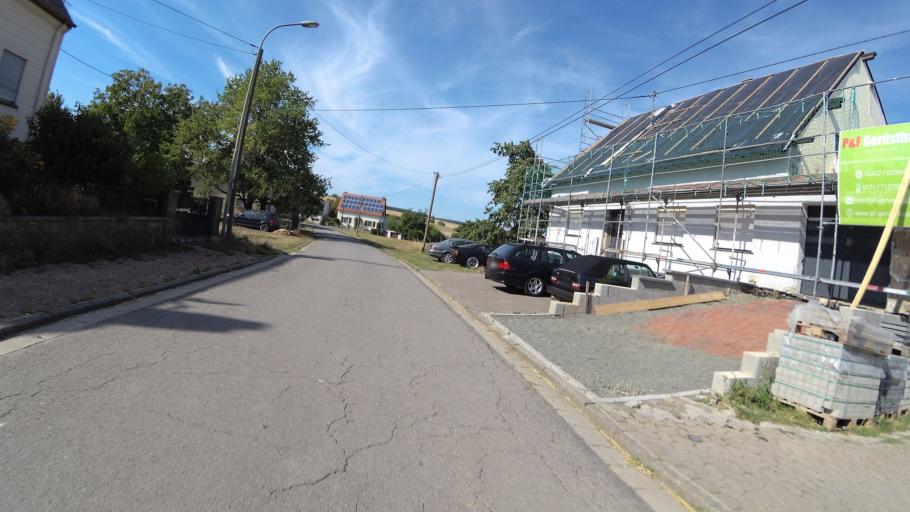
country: DE
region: Saarland
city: Gersheim
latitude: 49.1441
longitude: 7.2721
